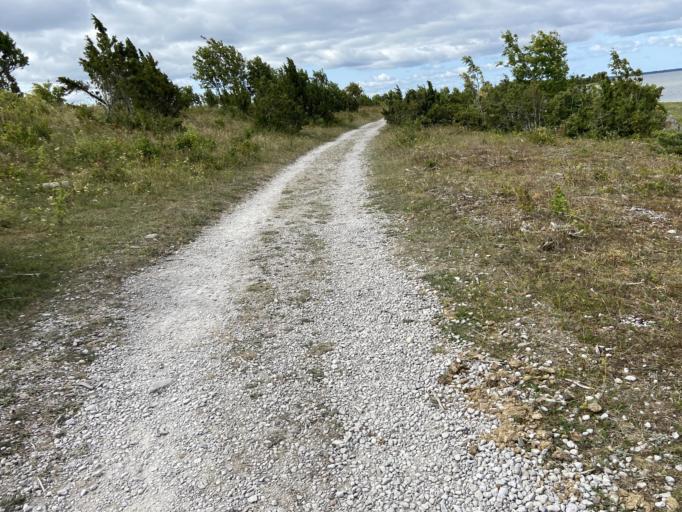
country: EE
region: Hiiumaa
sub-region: Kaerdla linn
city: Kardla
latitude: 58.7639
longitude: 22.8068
